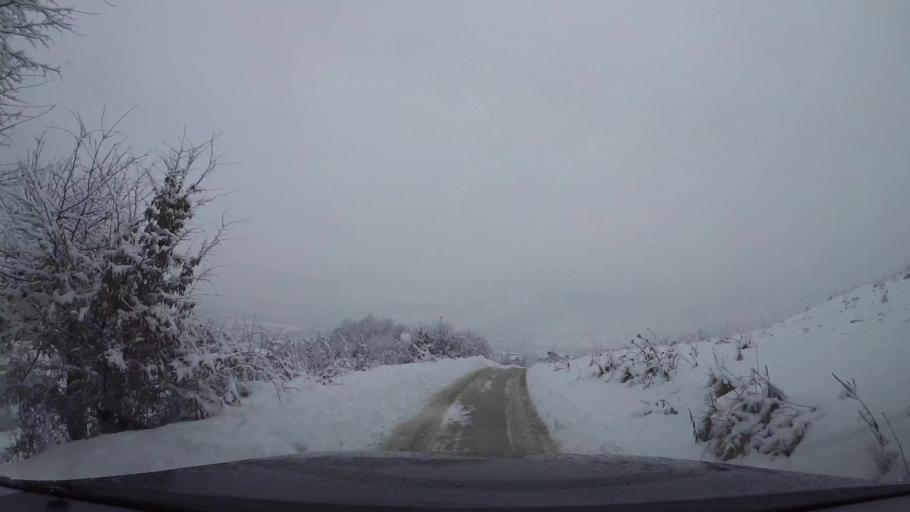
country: BA
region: Federation of Bosnia and Herzegovina
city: Vogosca
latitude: 43.8770
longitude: 18.3258
